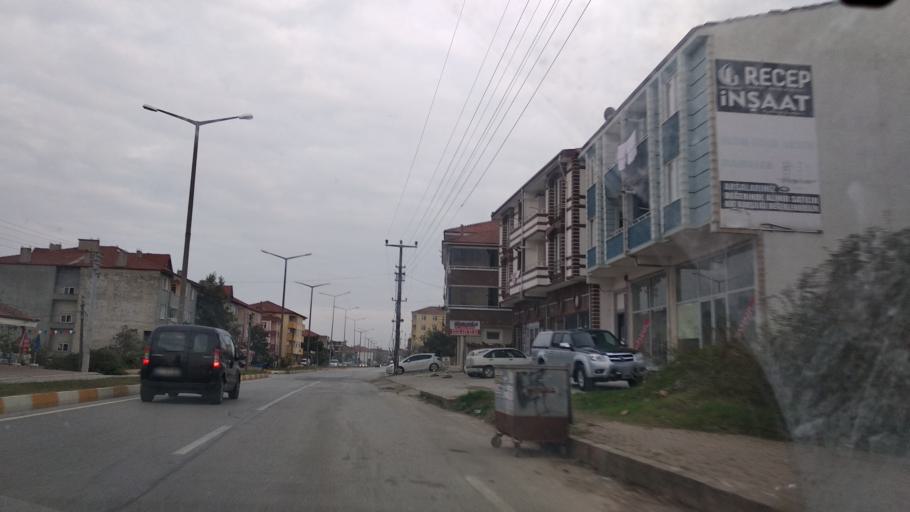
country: TR
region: Sakarya
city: Karasu
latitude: 41.0968
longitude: 30.6783
